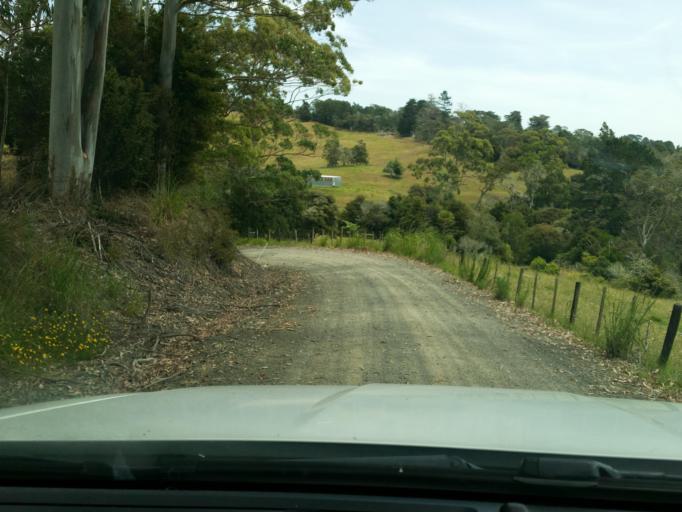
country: NZ
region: Northland
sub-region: Whangarei
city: Ruakaka
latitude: -36.0365
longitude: 174.2650
